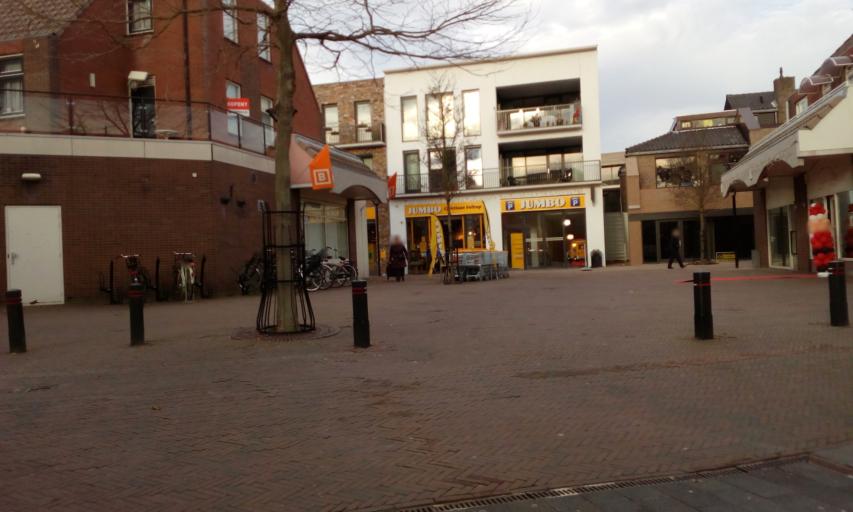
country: NL
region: South Holland
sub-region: Gemeente Lansingerland
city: Bergschenhoek
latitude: 51.9889
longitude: 4.5011
